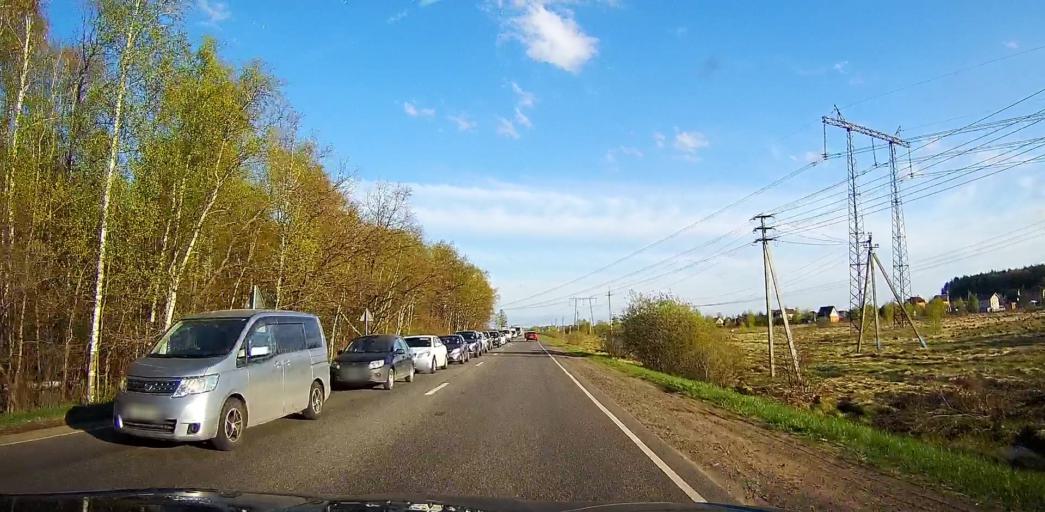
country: RU
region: Moskovskaya
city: Bronnitsy
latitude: 55.3765
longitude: 38.2113
